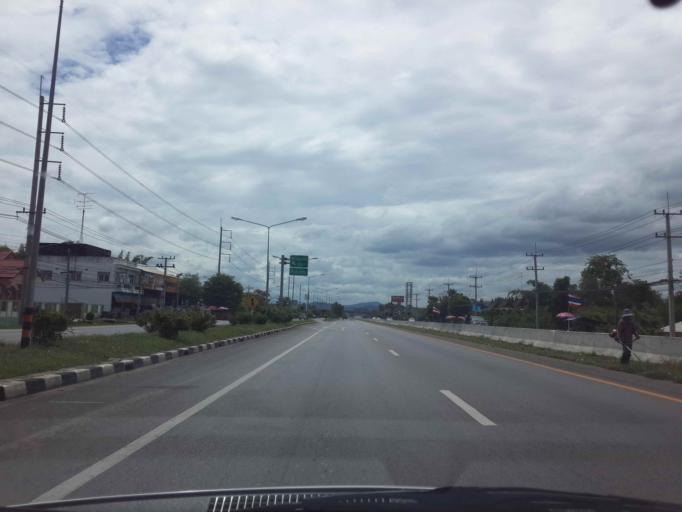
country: TH
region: Phetchaburi
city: Phetchaburi
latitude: 13.1190
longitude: 99.9019
